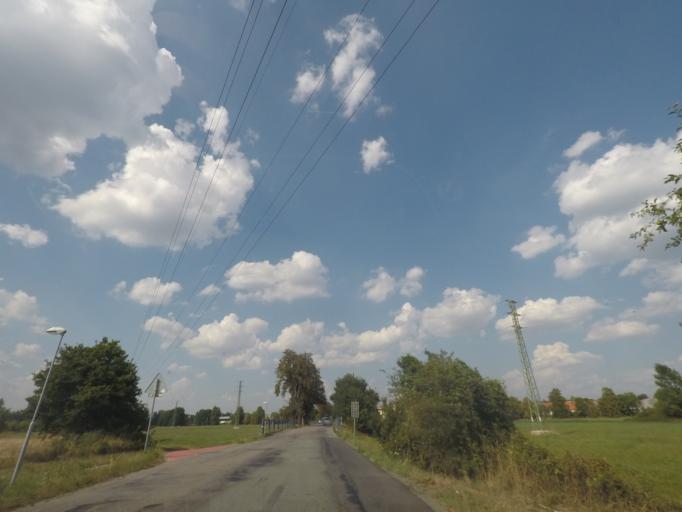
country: CZ
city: Albrechtice nad Orlici
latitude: 50.1459
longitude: 16.0652
